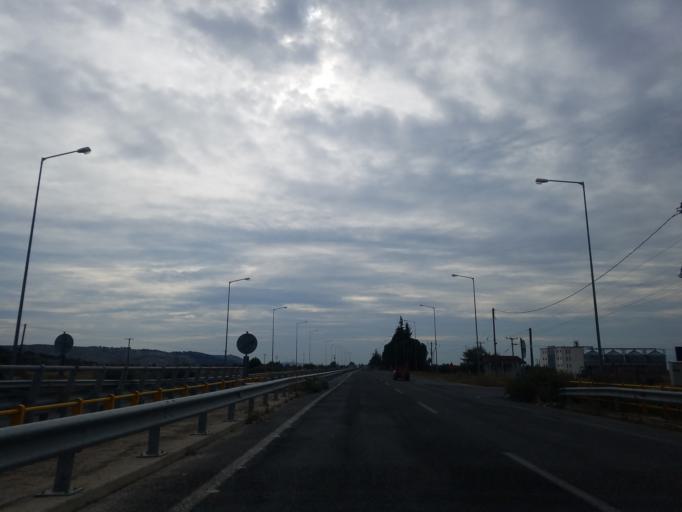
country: GR
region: Thessaly
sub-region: Trikala
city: Vasiliki
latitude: 39.6646
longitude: 21.6711
